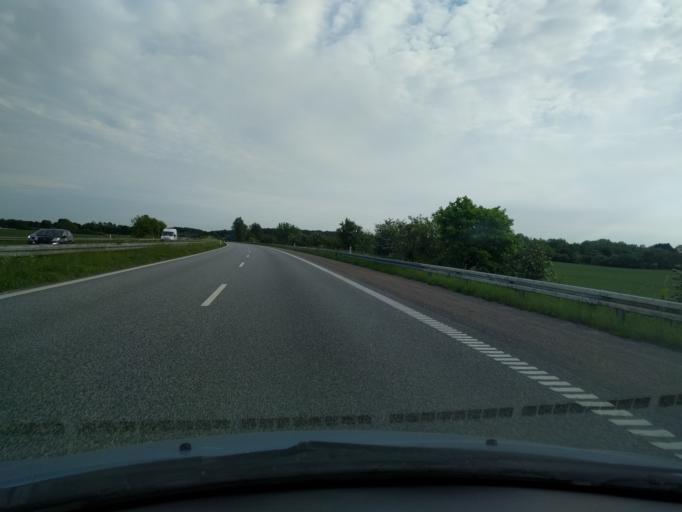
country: DK
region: Zealand
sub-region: Koge Kommune
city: Bjaeverskov
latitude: 55.3985
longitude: 12.0955
